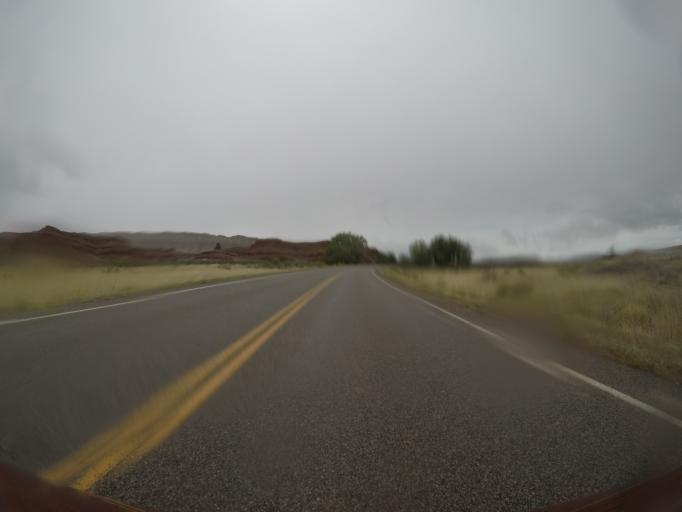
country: US
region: Wyoming
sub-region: Big Horn County
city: Lovell
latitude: 44.9661
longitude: -108.2735
